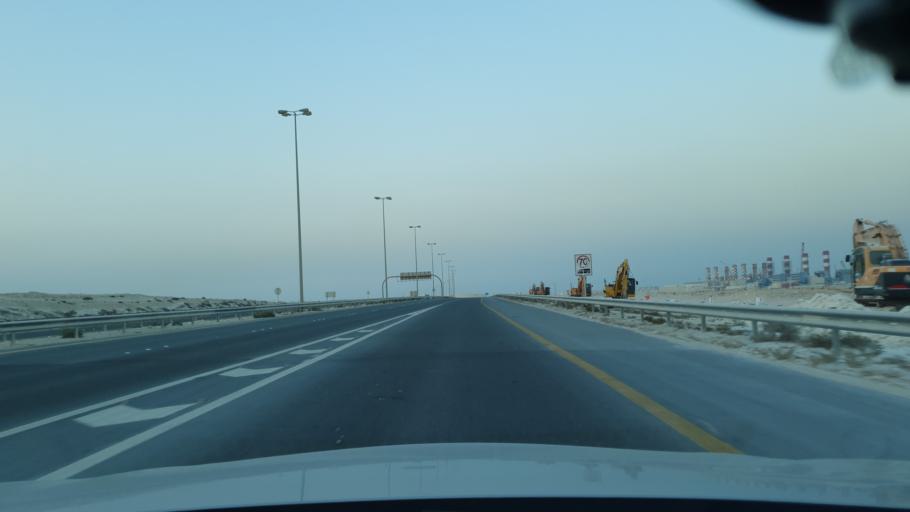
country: BH
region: Central Governorate
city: Dar Kulayb
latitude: 25.9606
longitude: 50.5969
